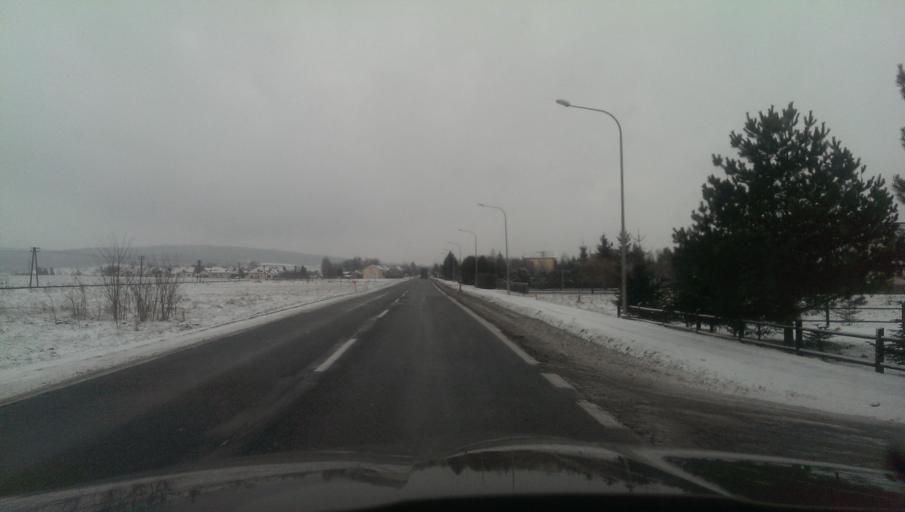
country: PL
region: Subcarpathian Voivodeship
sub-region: Powiat sanocki
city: Dlugie
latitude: 49.5801
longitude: 22.0347
